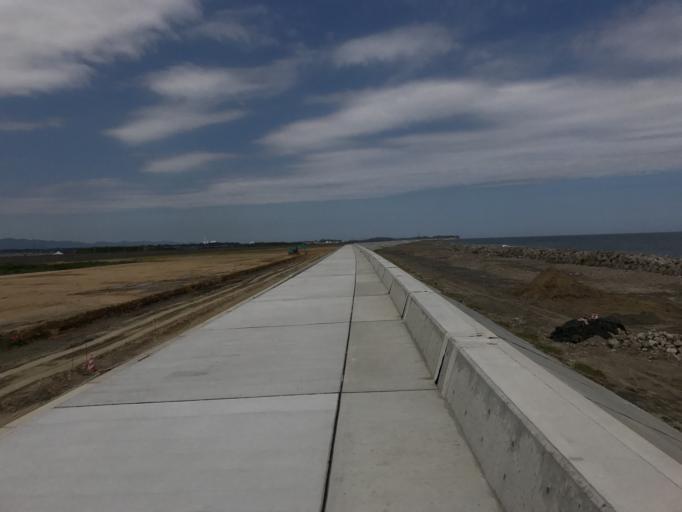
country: JP
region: Miyagi
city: Marumori
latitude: 37.7743
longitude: 140.9883
